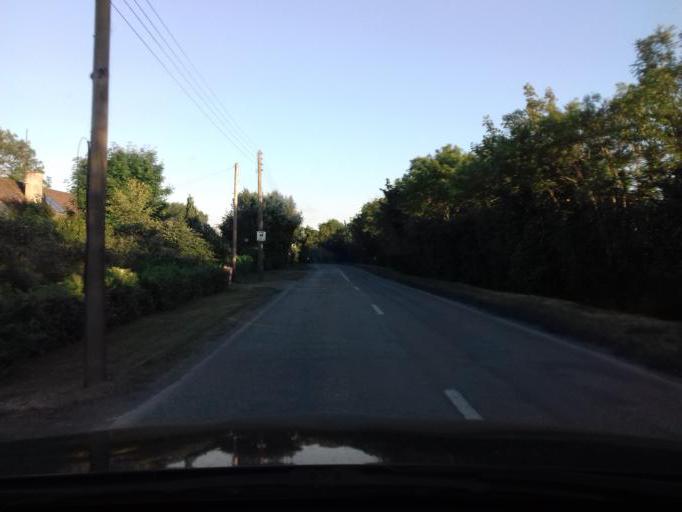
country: IE
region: Leinster
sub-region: Dublin City
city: Finglas
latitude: 53.4659
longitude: -6.3162
